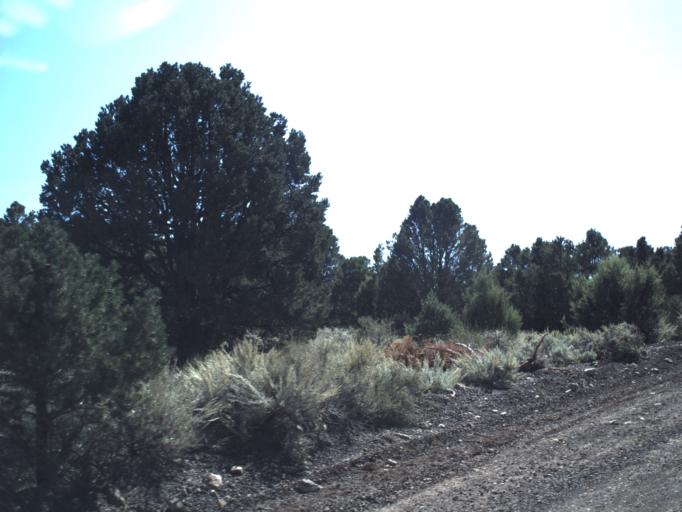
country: US
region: Utah
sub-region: Piute County
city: Junction
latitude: 38.2492
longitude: -112.3093
